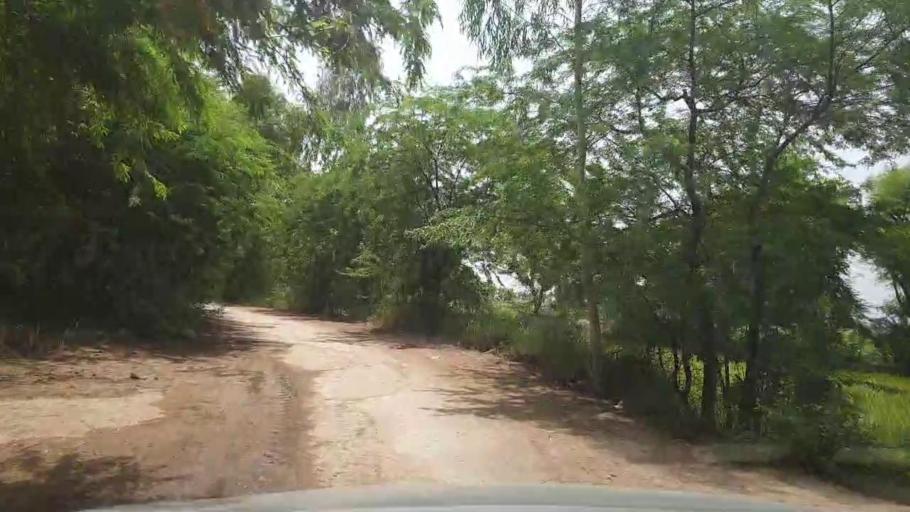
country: PK
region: Sindh
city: Garhi Yasin
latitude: 27.9278
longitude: 68.4013
